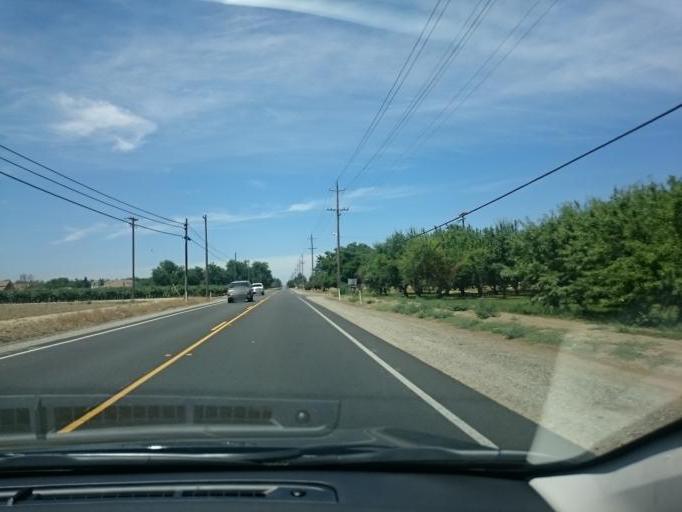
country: US
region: California
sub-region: Stanislaus County
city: Hughson
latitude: 37.6387
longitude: -120.8284
